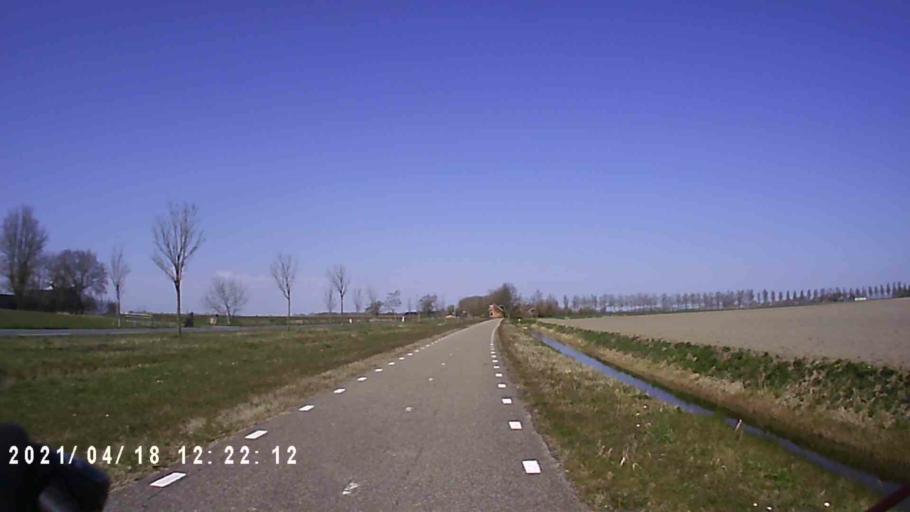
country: NL
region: Friesland
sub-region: Gemeente Kollumerland en Nieuwkruisland
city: Kollum
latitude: 53.3226
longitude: 6.1288
